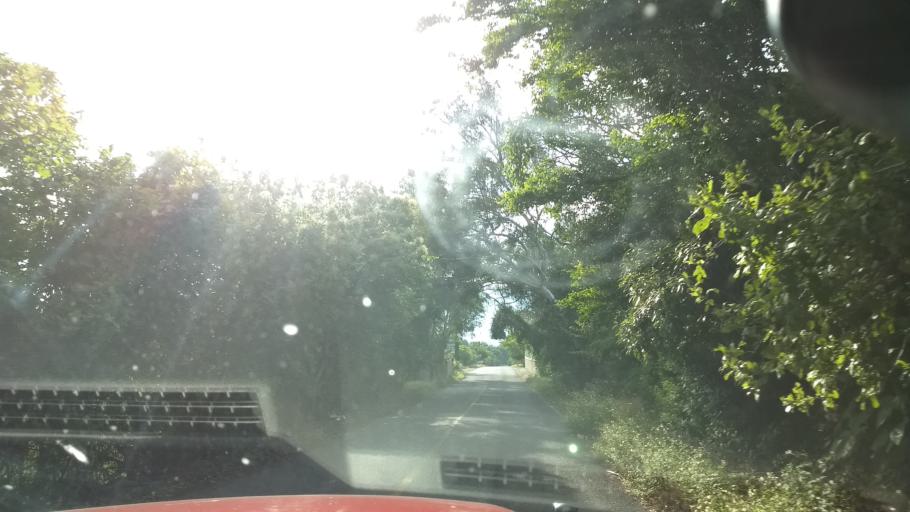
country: MX
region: Colima
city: Suchitlan
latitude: 19.4679
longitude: -103.7662
